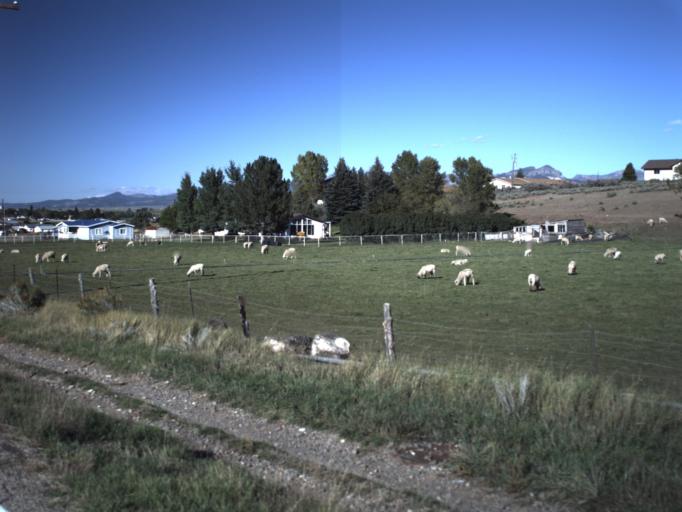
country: US
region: Utah
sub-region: Garfield County
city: Panguitch
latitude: 37.8058
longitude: -112.4353
